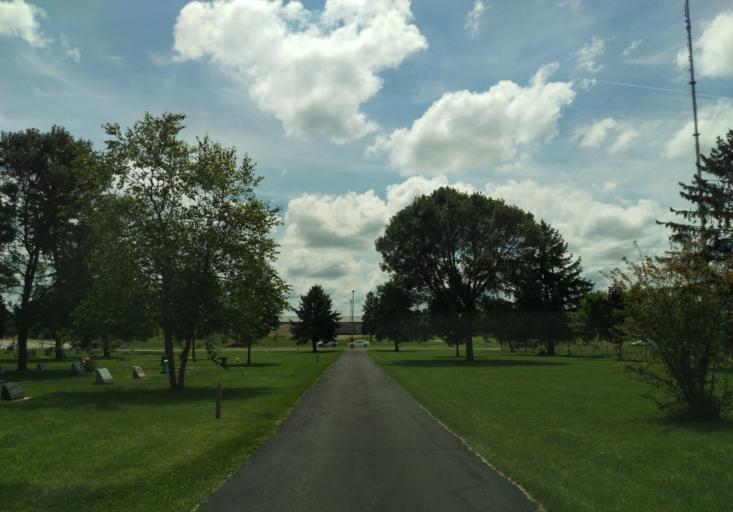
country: US
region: Wisconsin
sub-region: Dane County
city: Middleton
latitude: 43.0614
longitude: -89.5302
